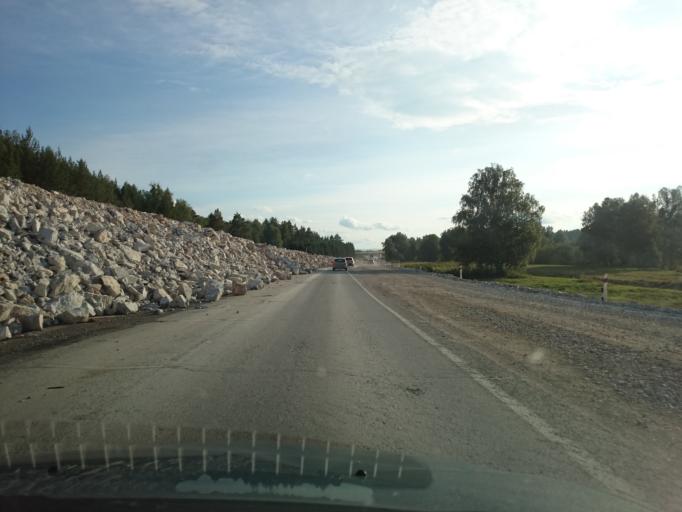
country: RU
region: Bashkortostan
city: Lomovka
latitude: 53.9103
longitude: 58.1771
